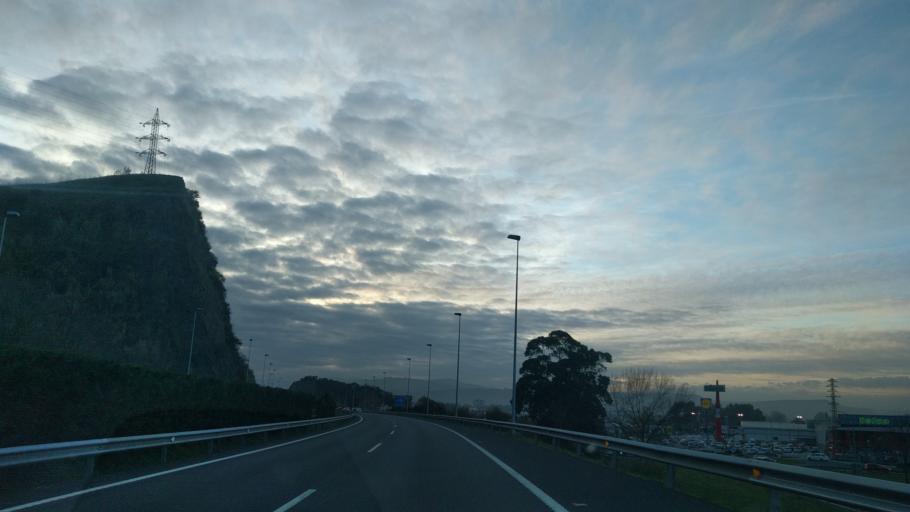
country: ES
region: Cantabria
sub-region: Provincia de Cantabria
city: Laredo
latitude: 43.4018
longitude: -3.4334
